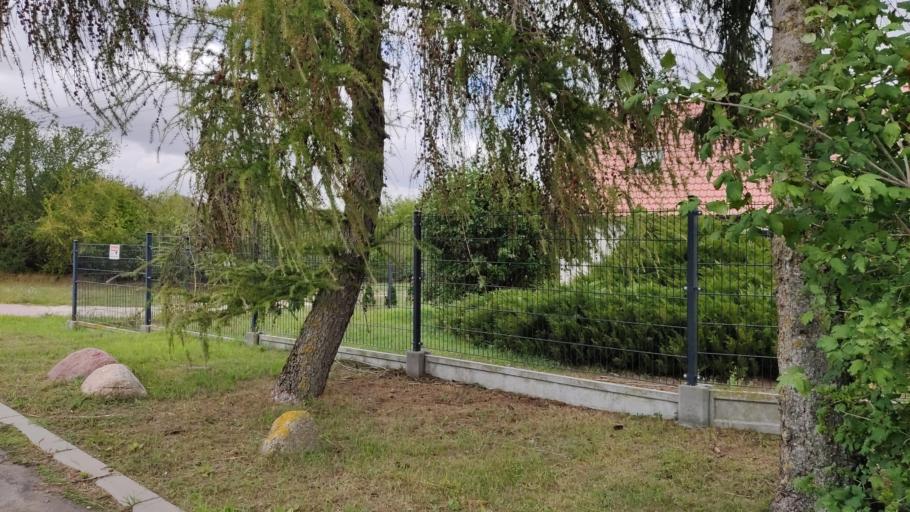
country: PL
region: Kujawsko-Pomorskie
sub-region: Powiat zninski
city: Barcin
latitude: 52.8436
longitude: 17.9537
